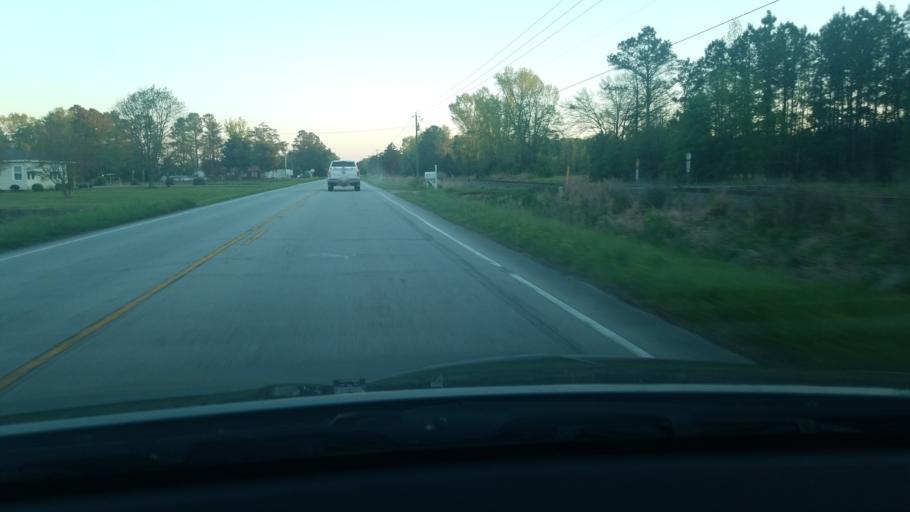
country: US
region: North Carolina
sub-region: Craven County
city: Vanceboro
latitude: 35.3476
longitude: -77.1510
